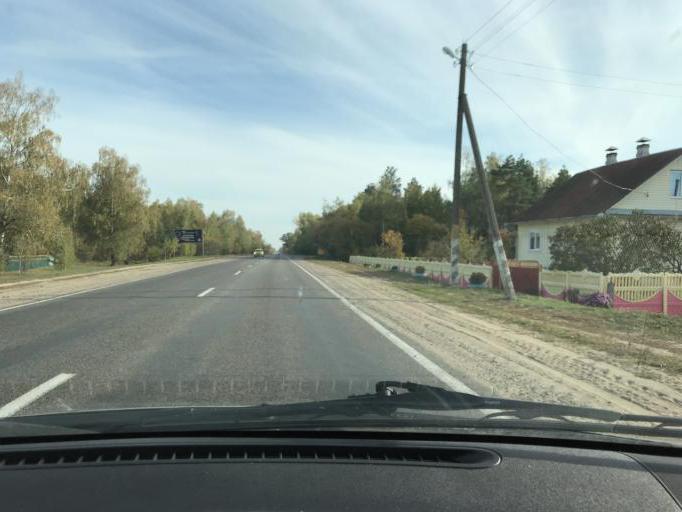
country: BY
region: Brest
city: Lahishyn
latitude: 52.2316
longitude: 26.0166
